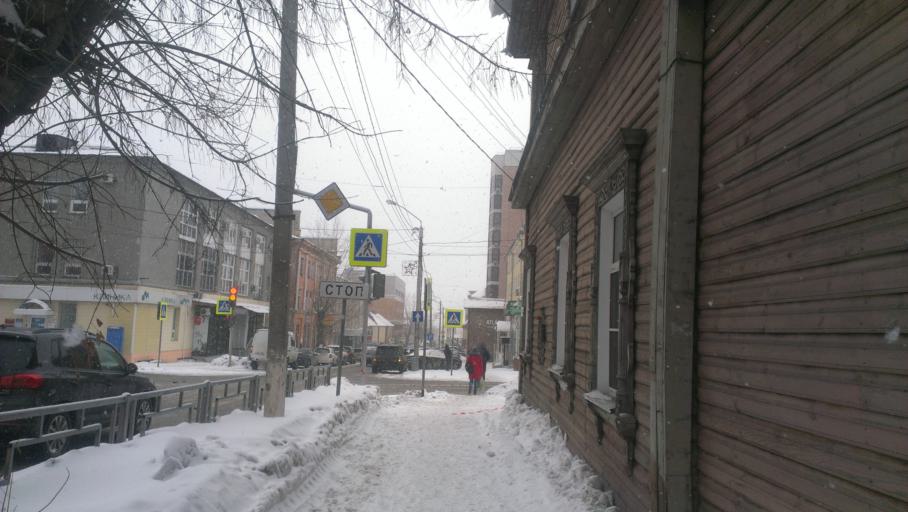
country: RU
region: Altai Krai
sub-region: Gorod Barnaulskiy
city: Barnaul
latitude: 53.3346
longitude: 83.7858
